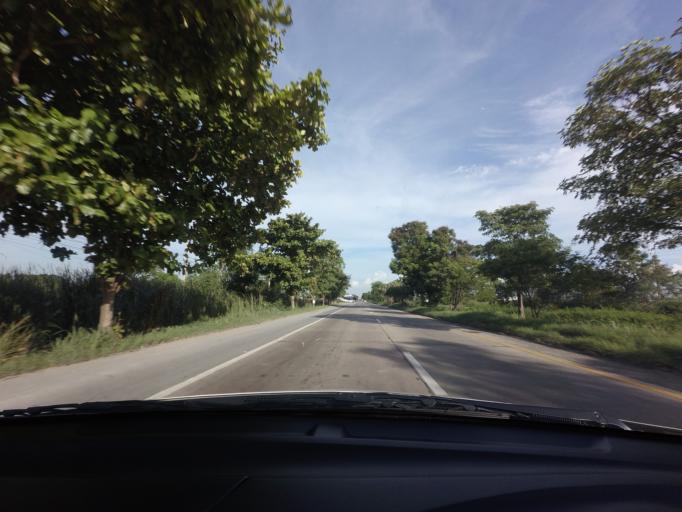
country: TH
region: Phra Nakhon Si Ayutthaya
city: Lat Bua Luang
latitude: 14.0776
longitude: 100.3171
